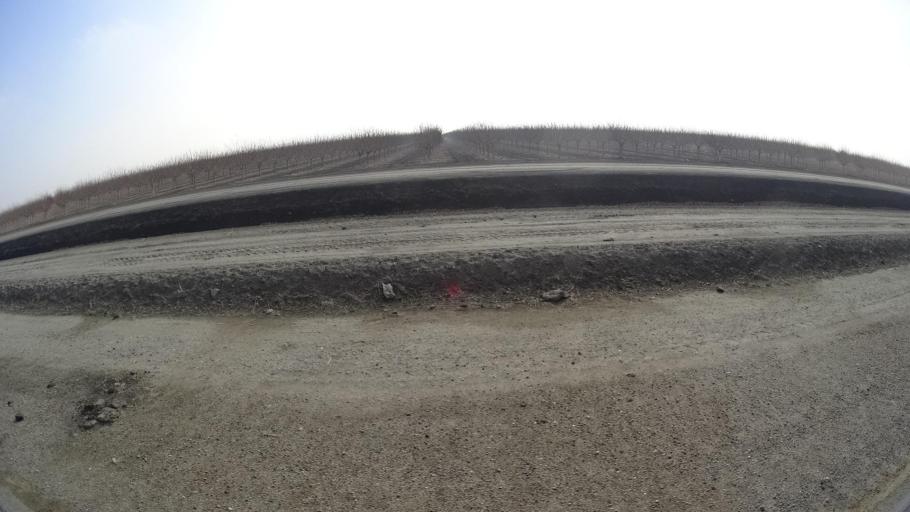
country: US
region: California
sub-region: Kern County
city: Greenfield
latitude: 35.1515
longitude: -119.0867
